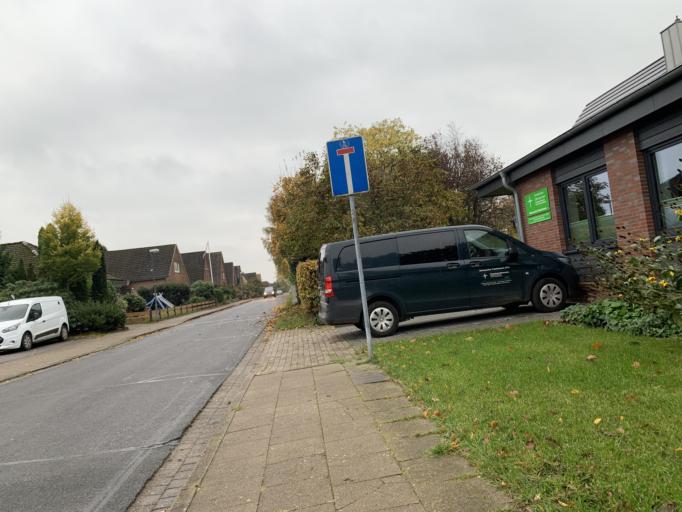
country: DE
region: Schleswig-Holstein
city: Wesseln
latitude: 54.1853
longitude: 9.0849
